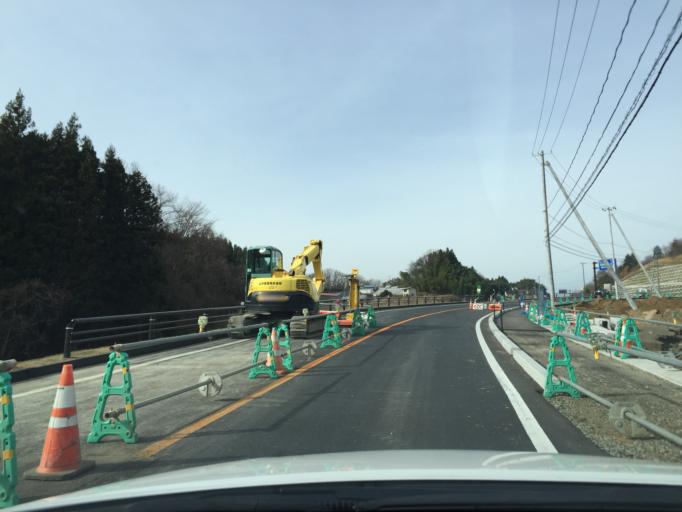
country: JP
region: Fukushima
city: Funehikimachi-funehiki
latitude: 37.4382
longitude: 140.5419
